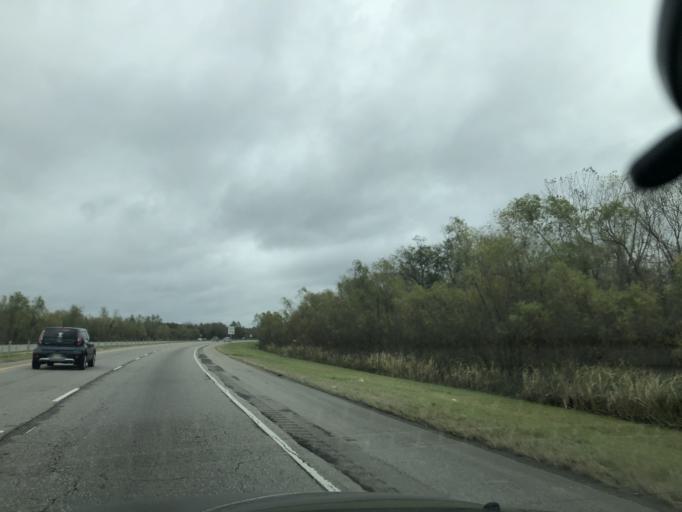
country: US
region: Louisiana
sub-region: Saint Charles Parish
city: Destrehan
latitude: 29.9620
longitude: -90.3604
